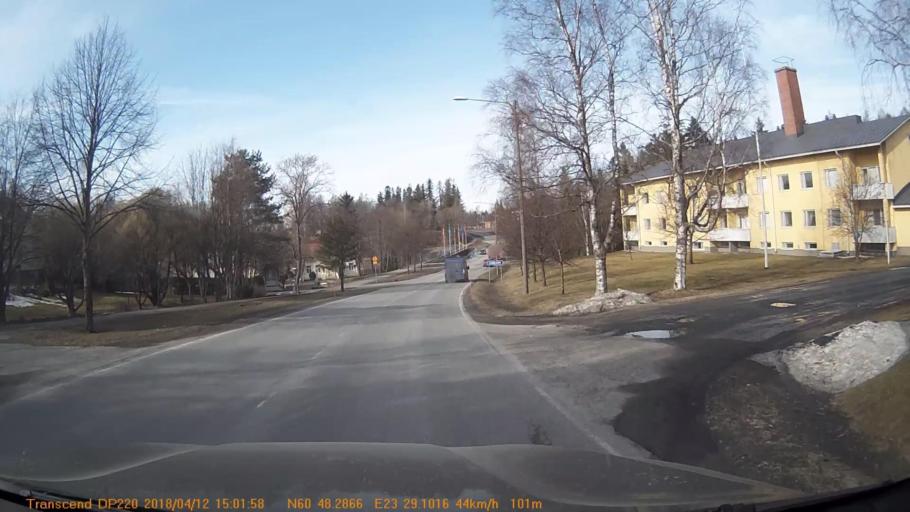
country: FI
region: Haeme
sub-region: Forssa
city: Jokioinen
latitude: 60.8048
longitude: 23.4851
